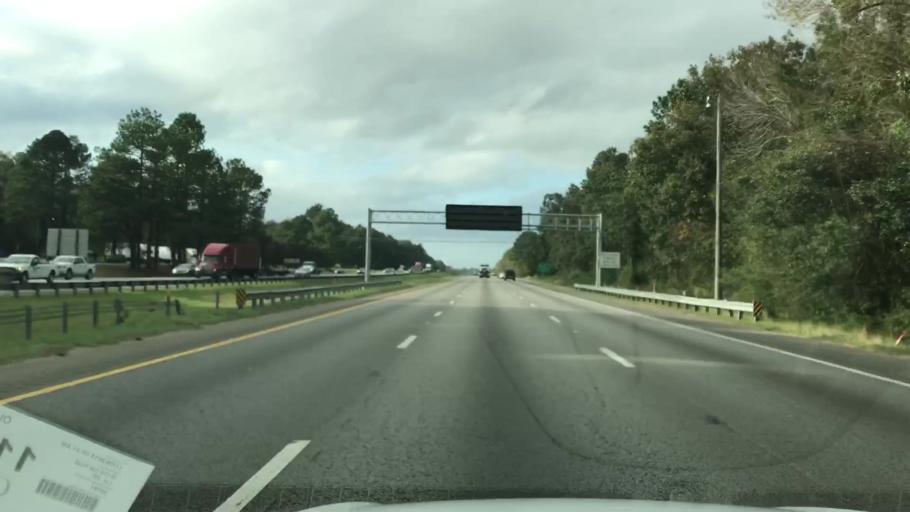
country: US
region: South Carolina
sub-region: Berkeley County
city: Ladson
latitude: 32.9884
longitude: -80.0829
